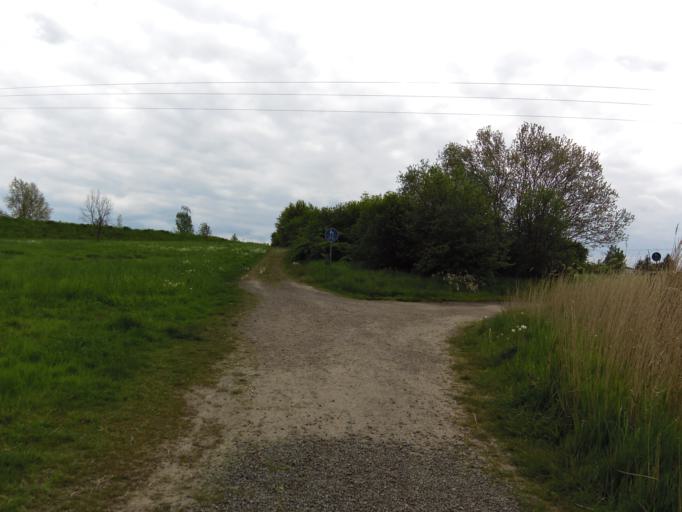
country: DE
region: Thuringia
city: Gotha
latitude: 50.9314
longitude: 10.7052
